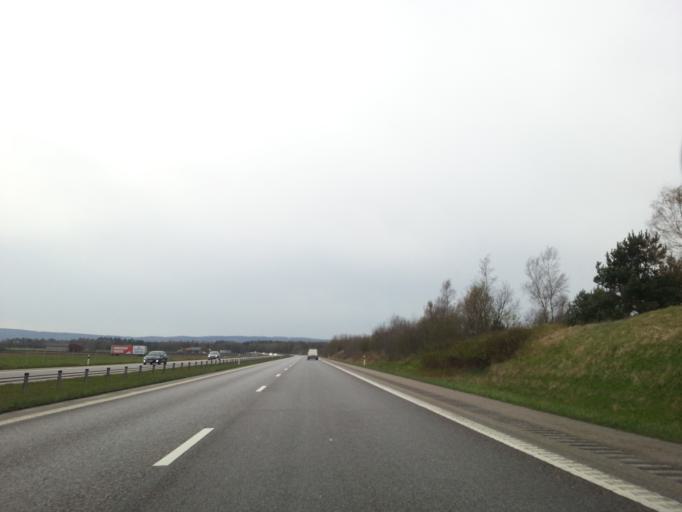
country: SE
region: Halland
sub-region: Laholms Kommun
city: Mellbystrand
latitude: 56.4769
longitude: 12.9443
